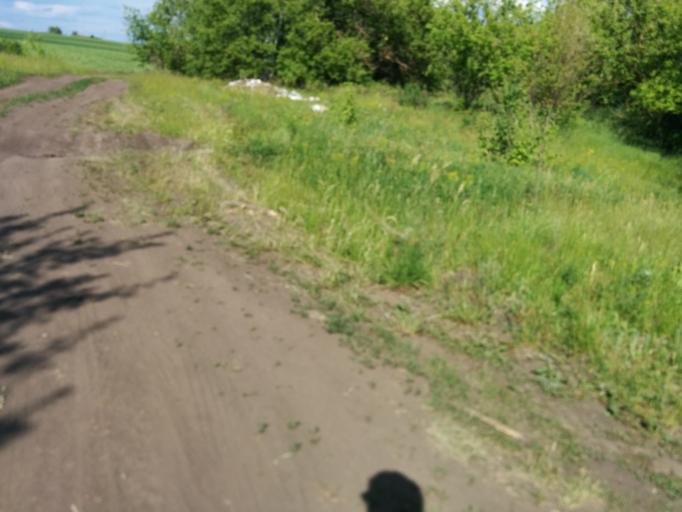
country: RU
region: Tambov
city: Tambov
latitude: 52.8057
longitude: 41.3918
